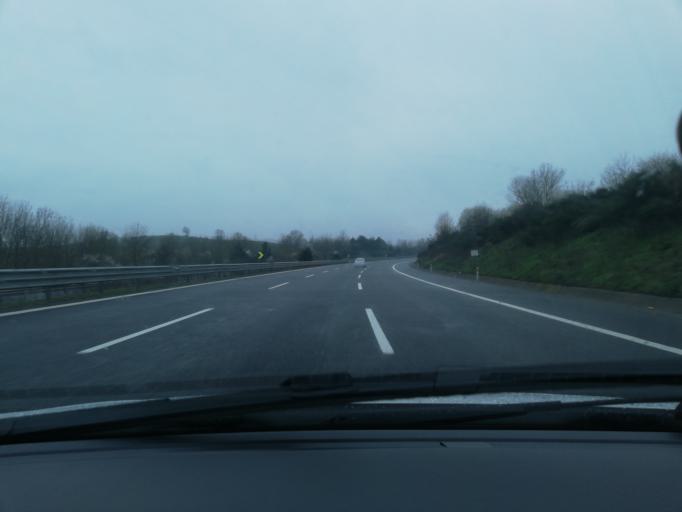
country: TR
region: Duzce
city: Gumusova
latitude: 40.8404
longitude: 30.9911
